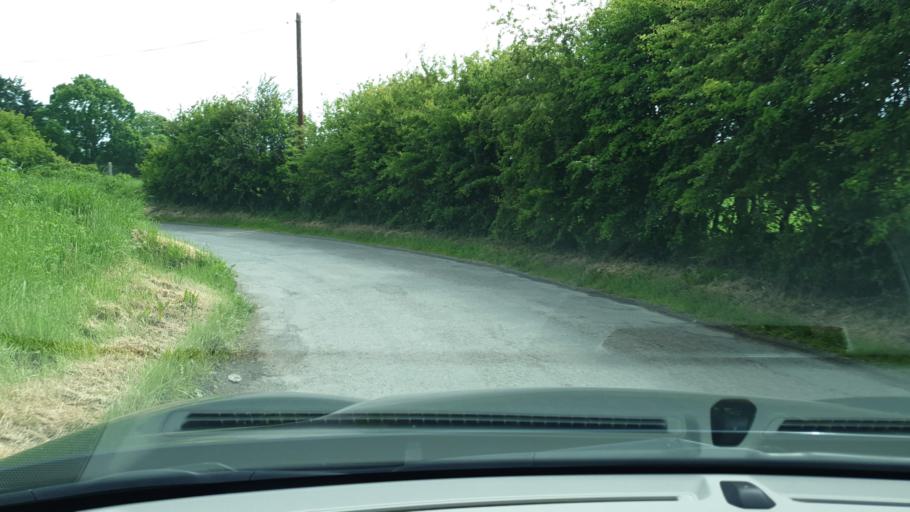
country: IE
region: Ulster
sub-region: An Cabhan
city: Kingscourt
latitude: 53.7983
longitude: -6.7229
